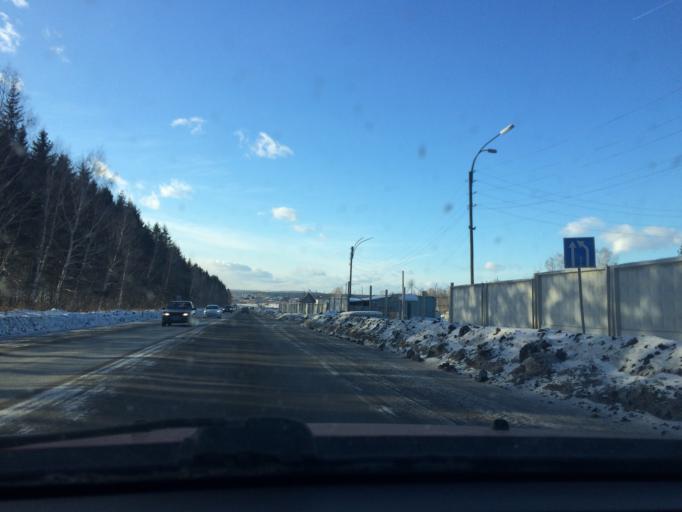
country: RU
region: Sverdlovsk
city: Aramil
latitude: 56.7717
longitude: 60.8647
